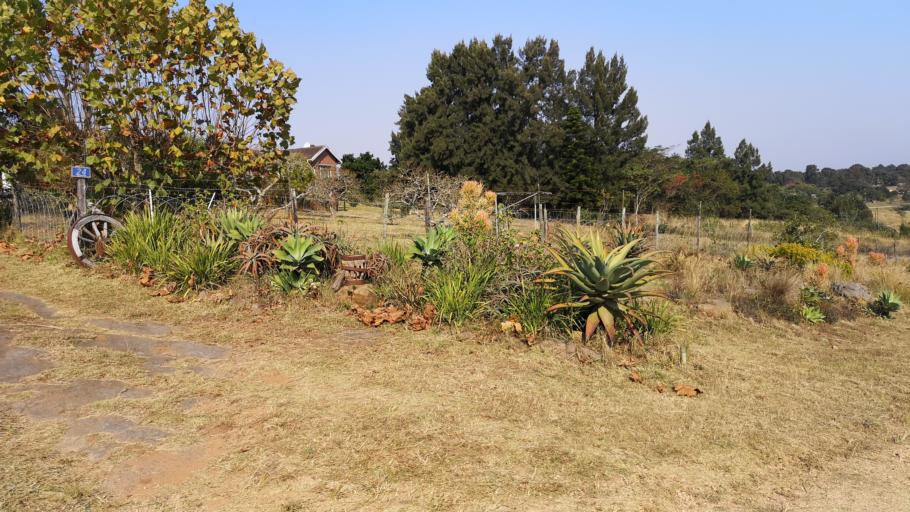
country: ZA
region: KwaZulu-Natal
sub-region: eThekwini Metropolitan Municipality
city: Mpumalanga
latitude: -29.7355
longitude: 30.6818
